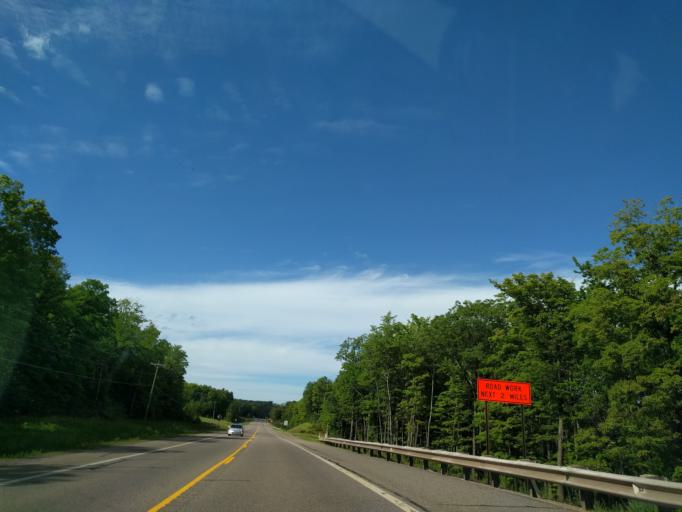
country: US
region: Michigan
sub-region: Marquette County
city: Harvey
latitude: 46.4800
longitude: -87.4173
